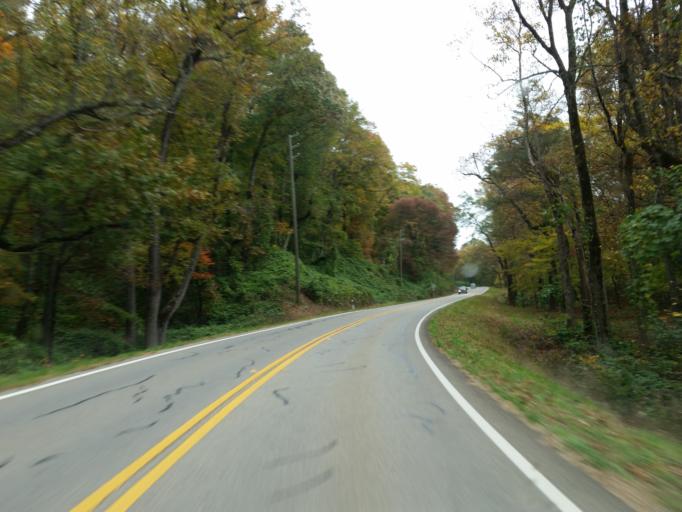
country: US
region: Georgia
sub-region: Pickens County
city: Jasper
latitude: 34.5346
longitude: -84.3885
